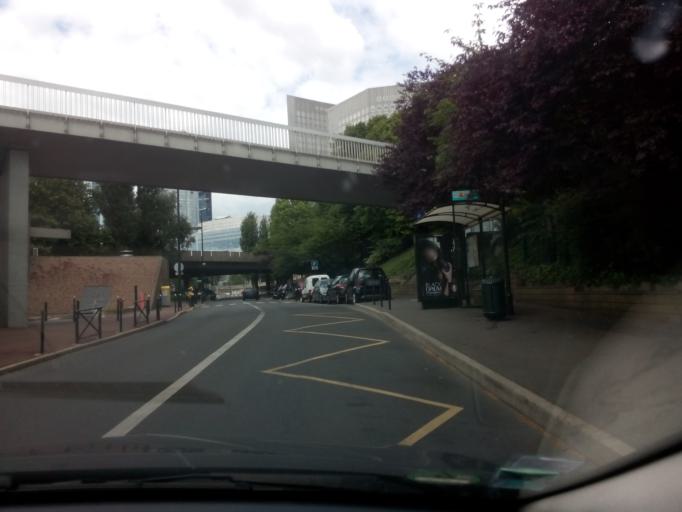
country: FR
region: Ile-de-France
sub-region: Departement des Hauts-de-Seine
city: Puteaux
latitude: 48.8869
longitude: 2.2381
